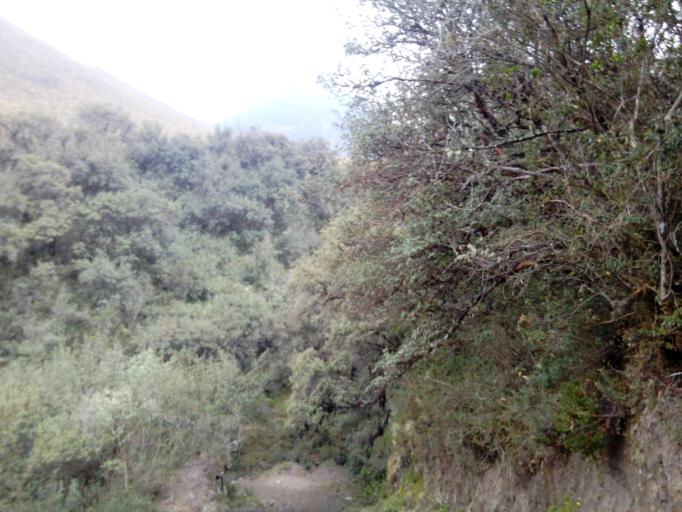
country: EC
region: Pichincha
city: Machachi
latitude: -0.5610
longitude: -78.5267
